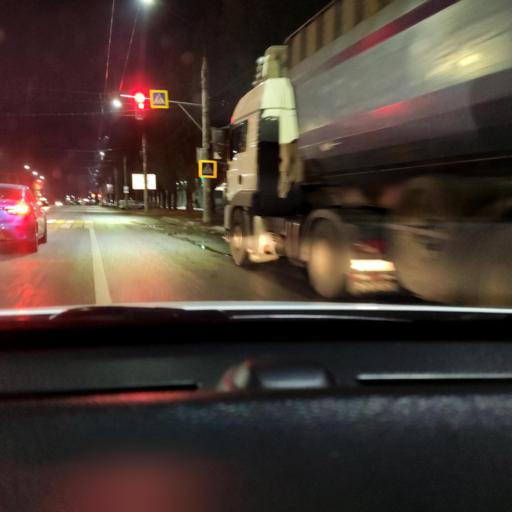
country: RU
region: Voronezj
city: Voronezh
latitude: 51.6816
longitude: 39.2615
